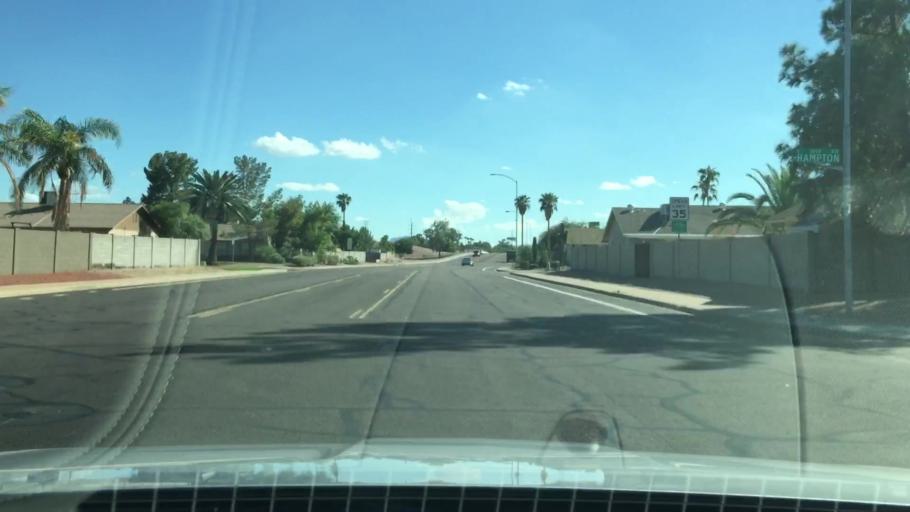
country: US
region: Arizona
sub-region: Maricopa County
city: Gilbert
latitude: 33.3901
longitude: -111.7474
